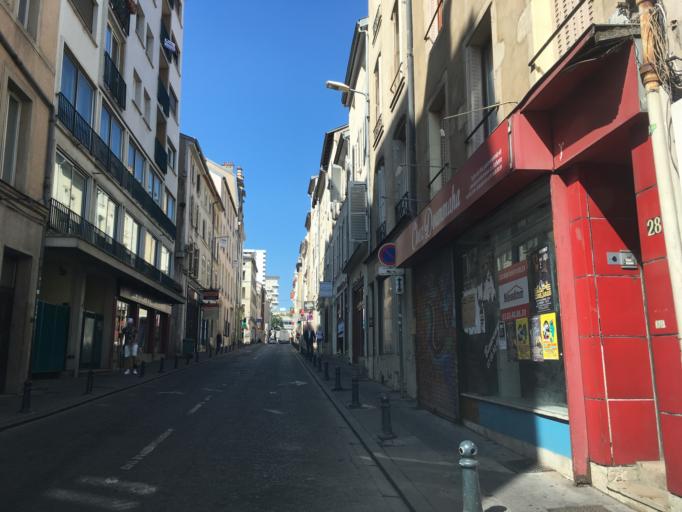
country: FR
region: Lorraine
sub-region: Departement de Meurthe-et-Moselle
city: Nancy
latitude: 48.6889
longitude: 6.1853
